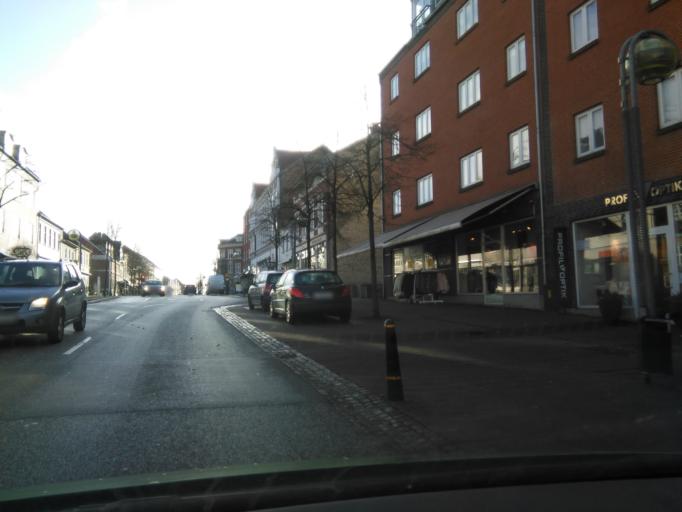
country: DK
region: Central Jutland
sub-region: Skanderborg Kommune
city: Skanderborg
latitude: 56.0359
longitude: 9.9315
